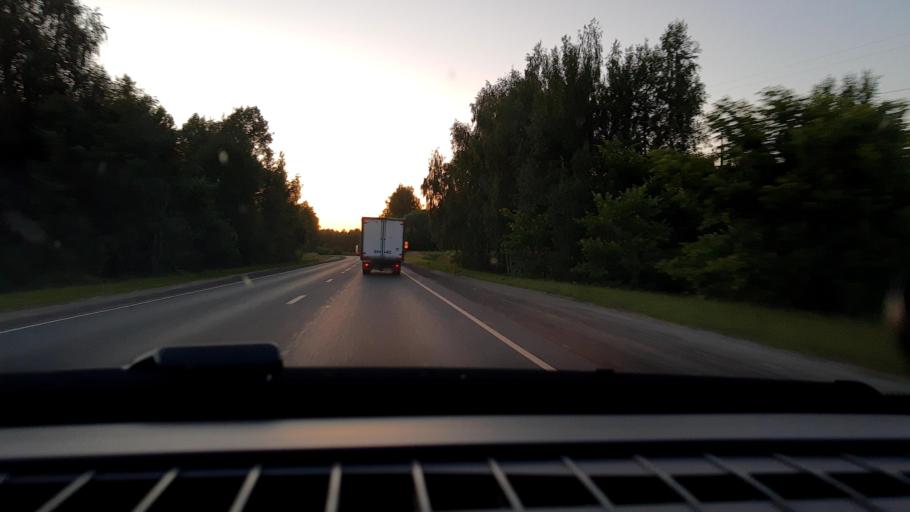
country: RU
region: Nizjnij Novgorod
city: Gorodets
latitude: 56.5835
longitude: 43.4710
